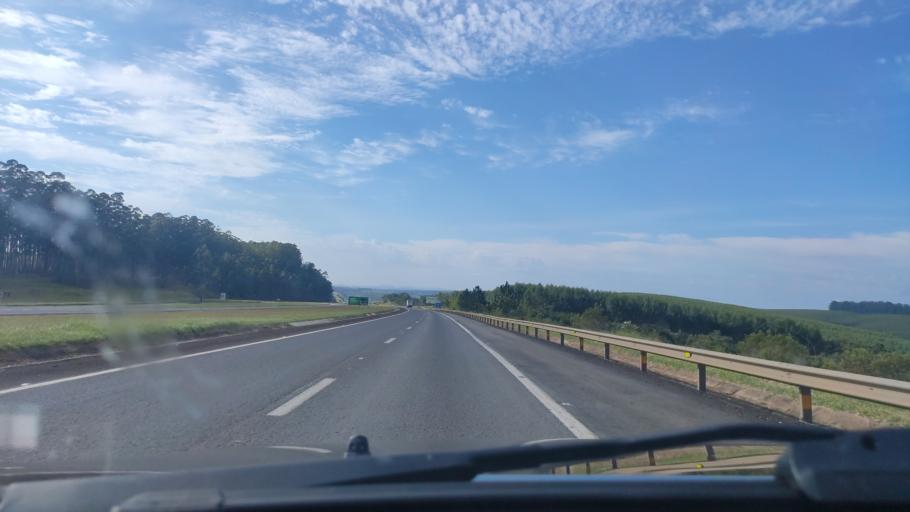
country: BR
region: Sao Paulo
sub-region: Itatinga
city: Itatinga
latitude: -23.1148
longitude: -48.4957
